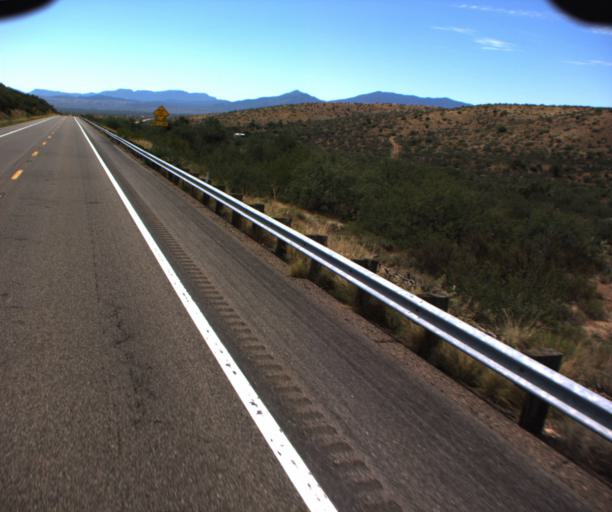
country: US
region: Arizona
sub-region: Gila County
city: Globe
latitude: 33.4576
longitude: -110.7211
